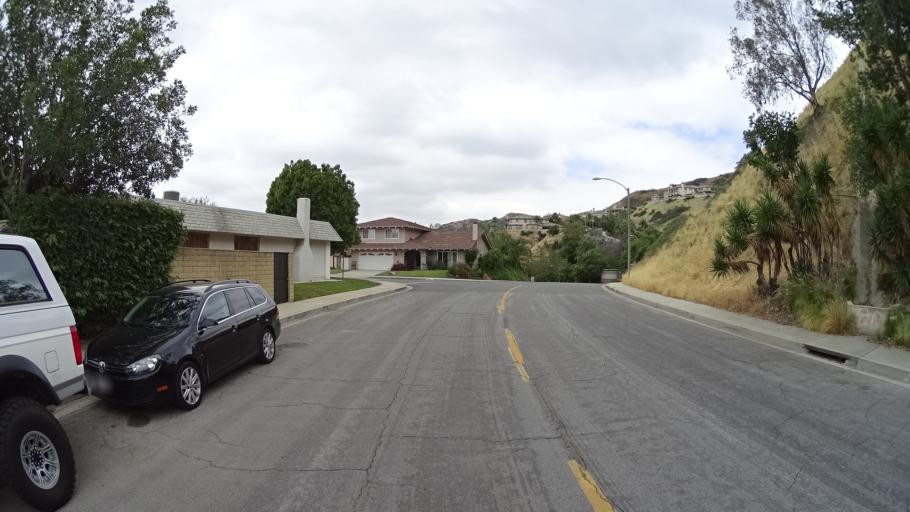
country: US
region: California
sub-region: Los Angeles County
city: Burbank
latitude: 34.2135
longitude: -118.3268
